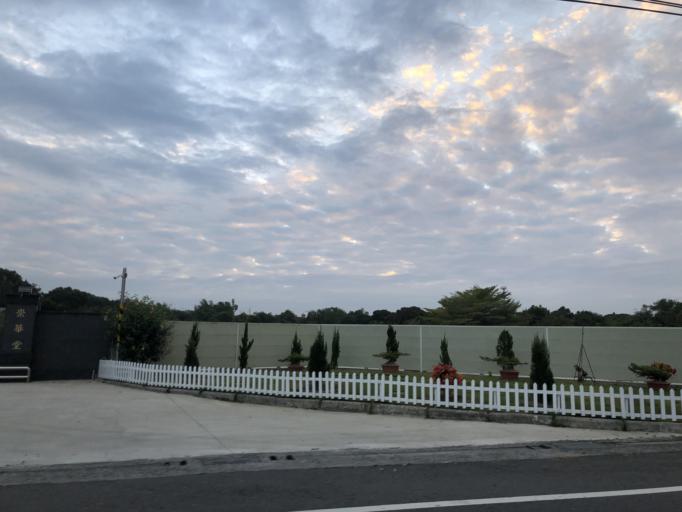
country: TW
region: Taiwan
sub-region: Tainan
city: Tainan
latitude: 23.0255
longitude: 120.3367
